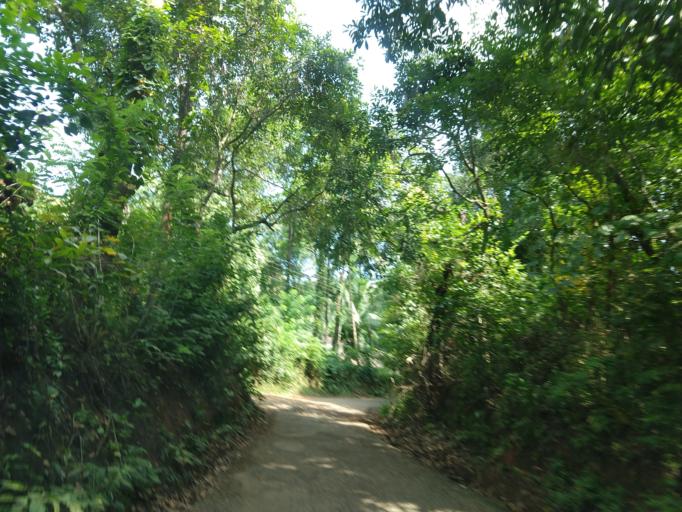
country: IN
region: Maharashtra
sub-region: Sindhudurg
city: Kudal
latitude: 16.0399
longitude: 73.6824
